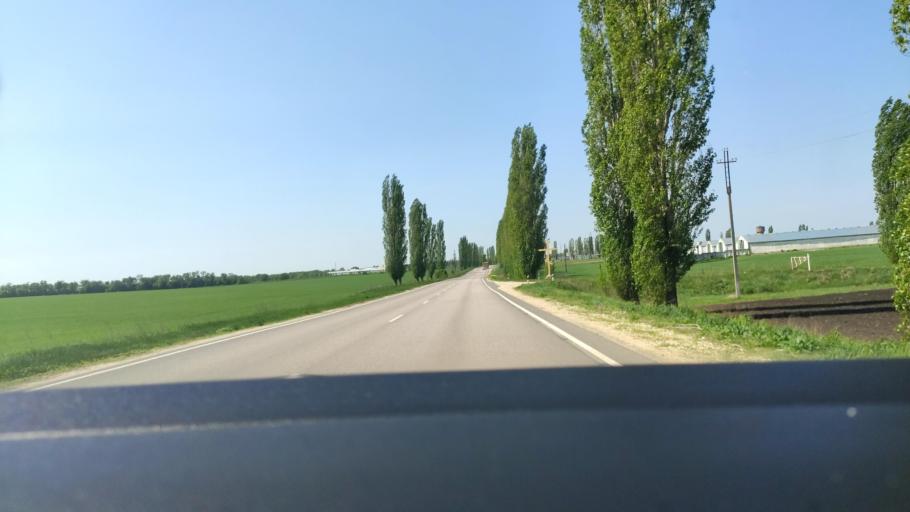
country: RU
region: Voronezj
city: Novaya Usman'
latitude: 51.5481
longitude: 39.3641
